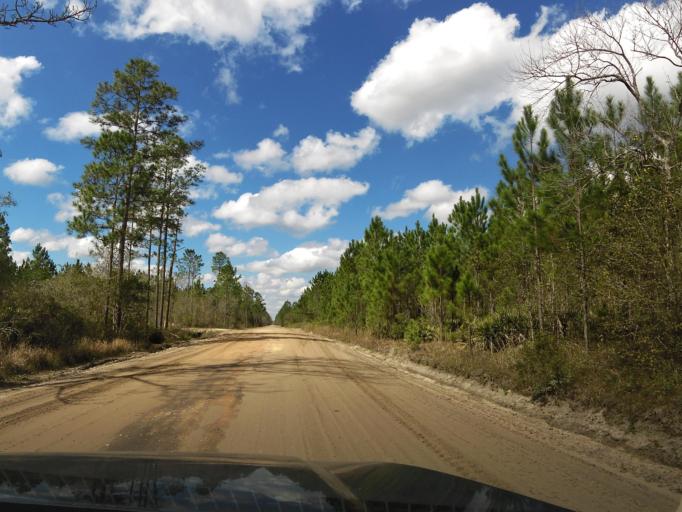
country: US
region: Florida
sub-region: Clay County
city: Green Cove Springs
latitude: 29.8369
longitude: -81.7740
